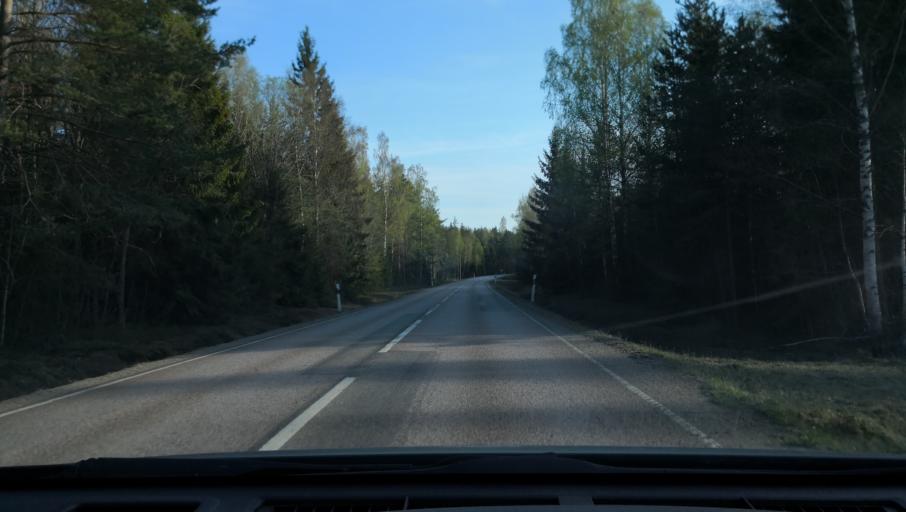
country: SE
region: Uppsala
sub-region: Heby Kommun
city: Heby
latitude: 60.0059
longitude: 16.8373
